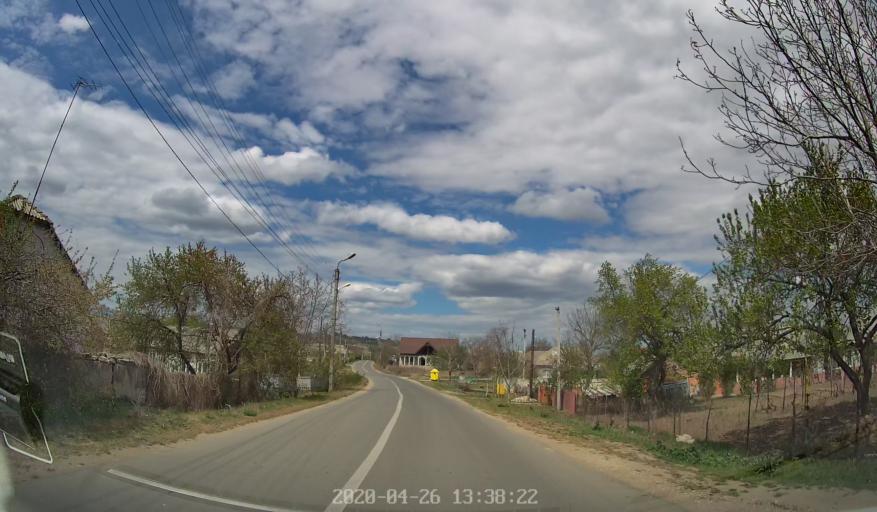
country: MD
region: Criuleni
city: Criuleni
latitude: 47.2075
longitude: 29.1671
